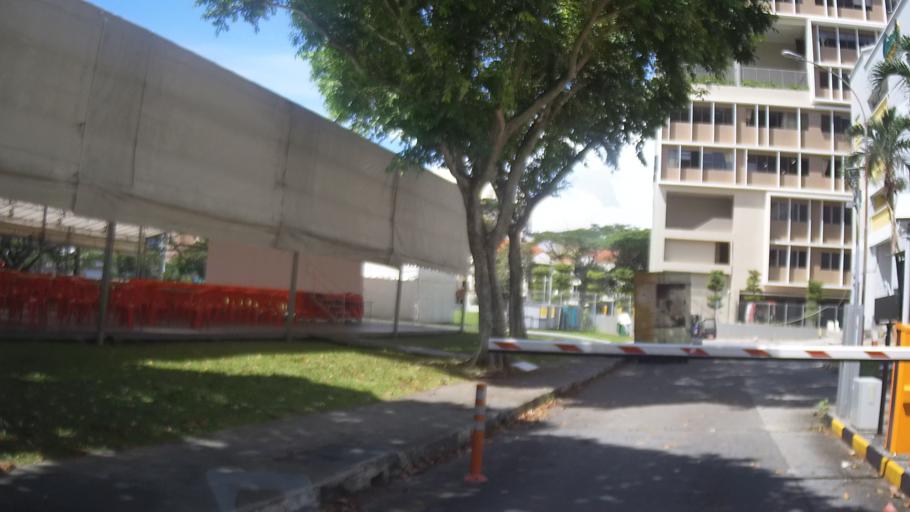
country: SG
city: Singapore
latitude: 1.3203
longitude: 103.8878
